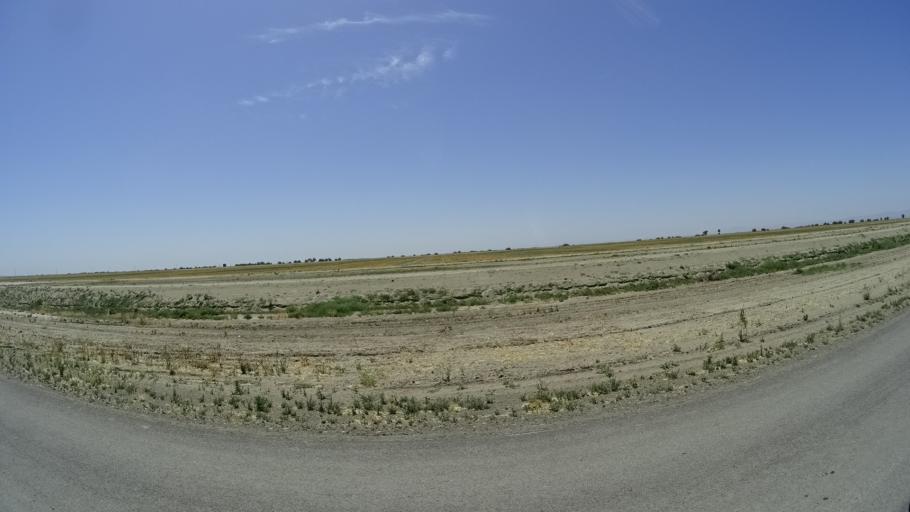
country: US
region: California
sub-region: Kings County
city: Stratford
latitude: 36.1526
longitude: -119.7240
